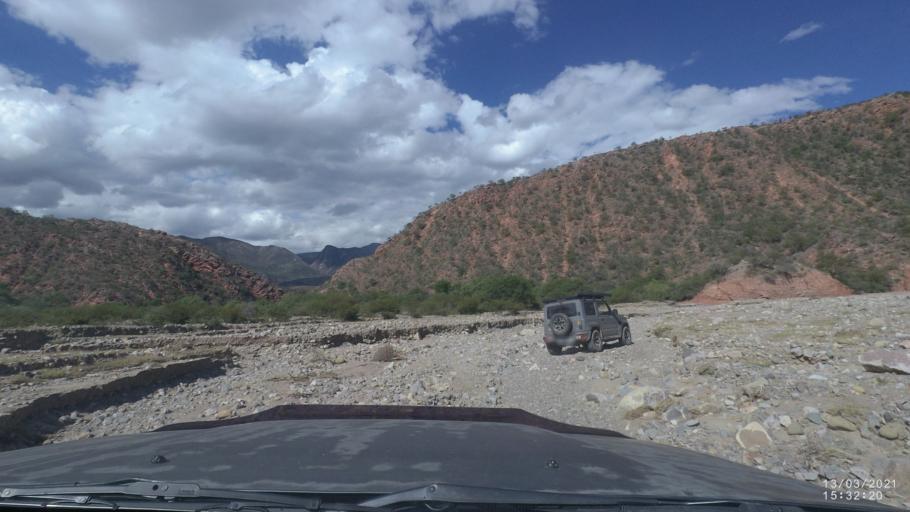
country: BO
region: Cochabamba
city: Cliza
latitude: -17.9488
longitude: -65.8542
